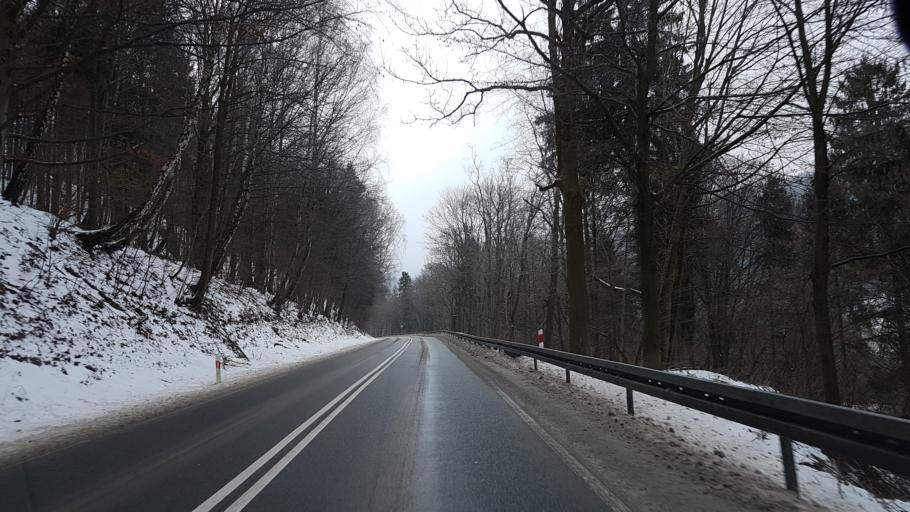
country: PL
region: Lesser Poland Voivodeship
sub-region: Powiat nowosadecki
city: Piwniczna-Zdroj
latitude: 49.4066
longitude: 20.7460
